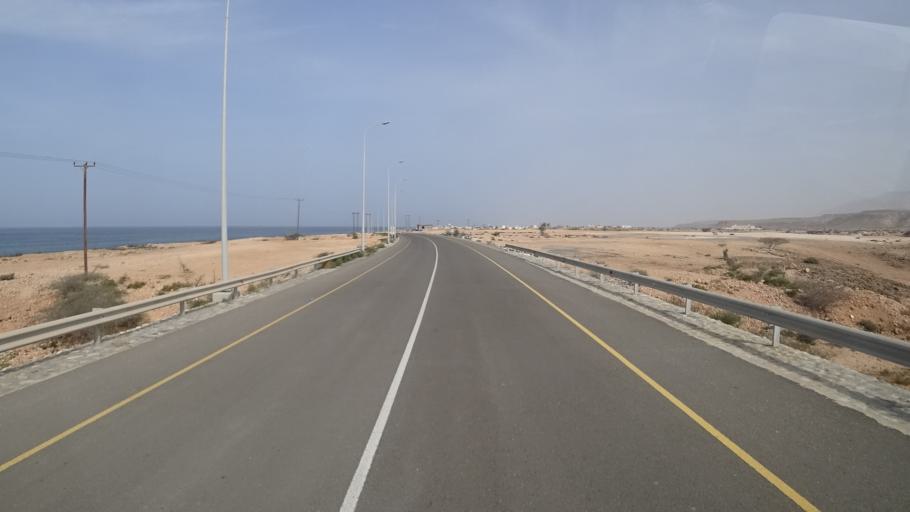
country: OM
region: Ash Sharqiyah
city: Sur
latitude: 22.9990
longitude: 59.1213
